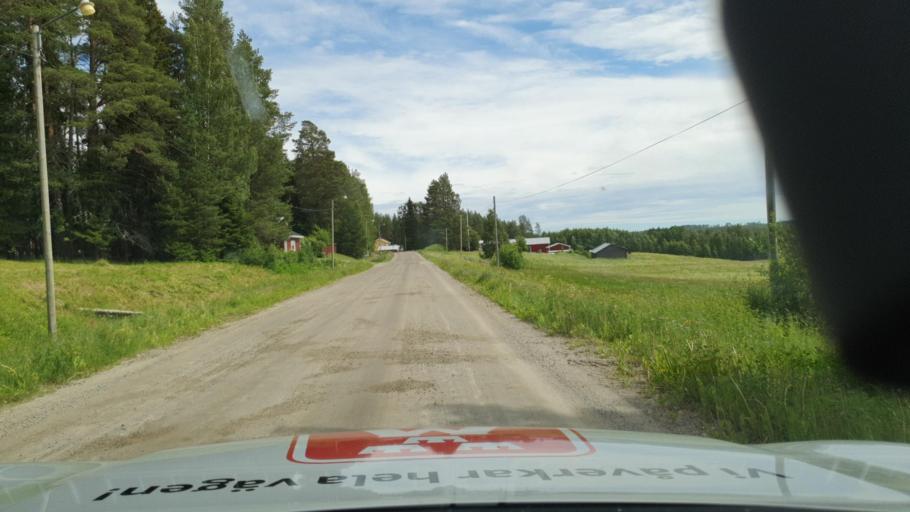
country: SE
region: Vaesterbotten
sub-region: Skelleftea Kommun
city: Burtraesk
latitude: 64.4899
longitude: 20.6069
